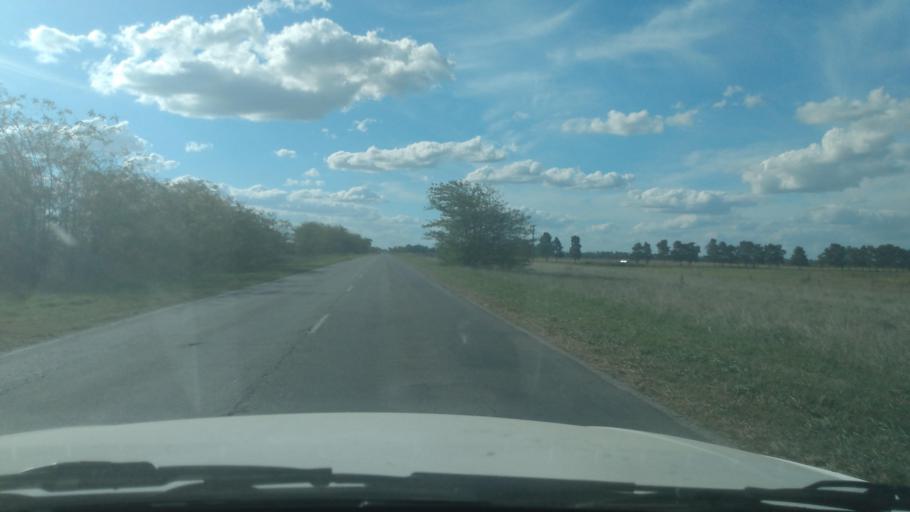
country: AR
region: Buenos Aires
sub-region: Partido de Navarro
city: Navarro
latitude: -34.9726
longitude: -59.3172
